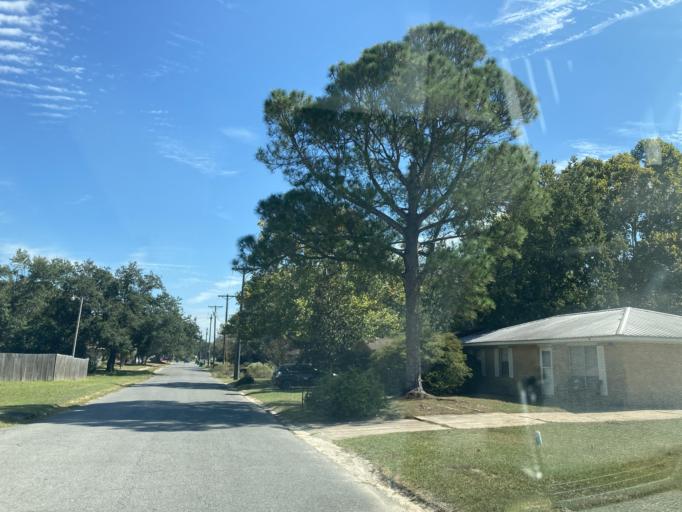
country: US
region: Mississippi
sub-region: Jackson County
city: Saint Martin
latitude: 30.4506
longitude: -88.8772
